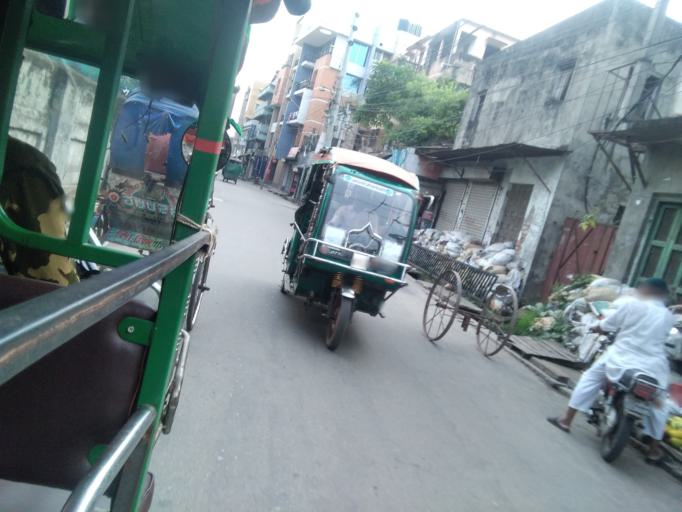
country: BD
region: Khulna
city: Khulna
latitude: 22.8142
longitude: 89.5617
